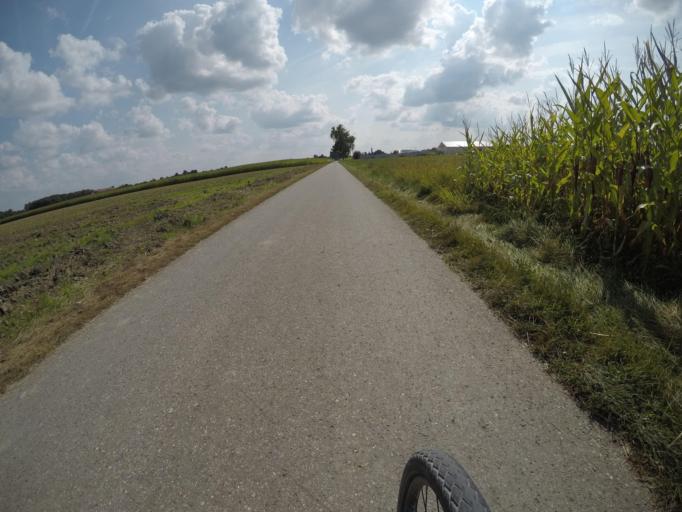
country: DE
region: Bavaria
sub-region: Swabia
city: Nordendorf
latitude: 48.5835
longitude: 10.8359
